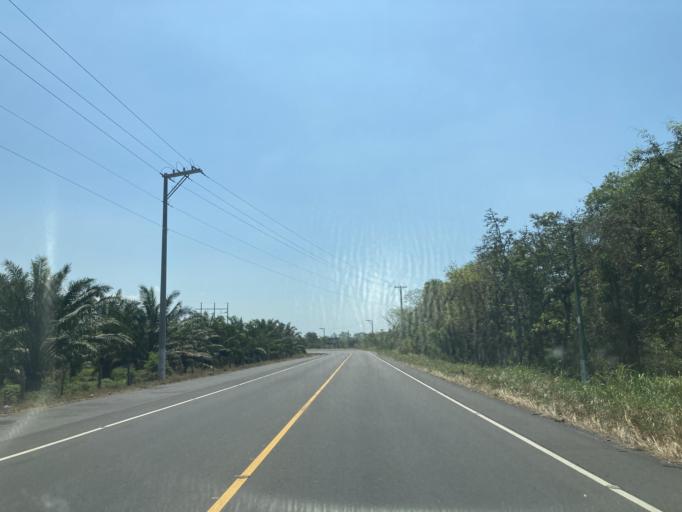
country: GT
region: Escuintla
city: Guanagazapa
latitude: 14.1092
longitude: -90.6319
